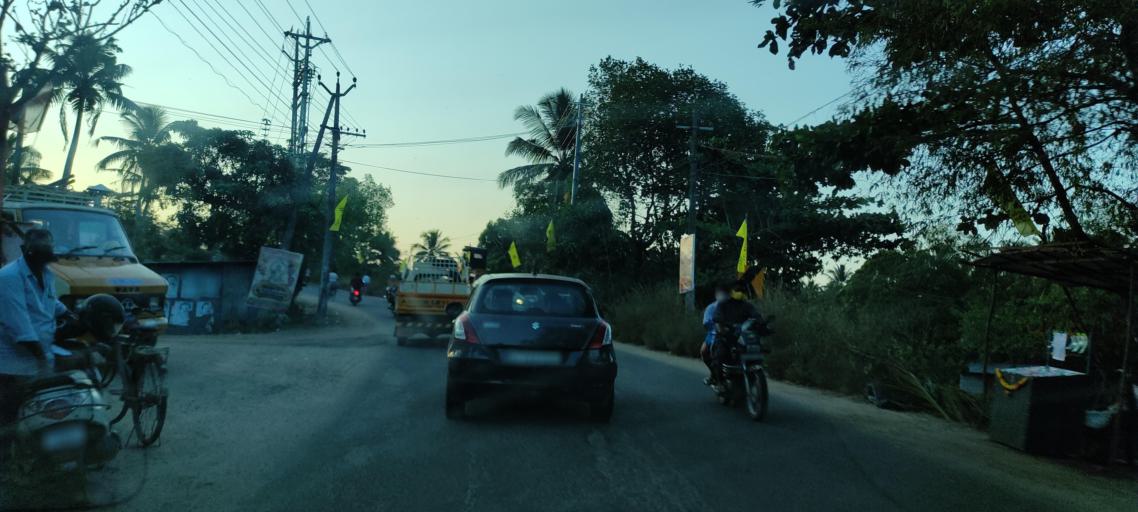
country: IN
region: Kerala
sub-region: Alappuzha
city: Kayankulam
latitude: 9.2588
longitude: 76.4138
